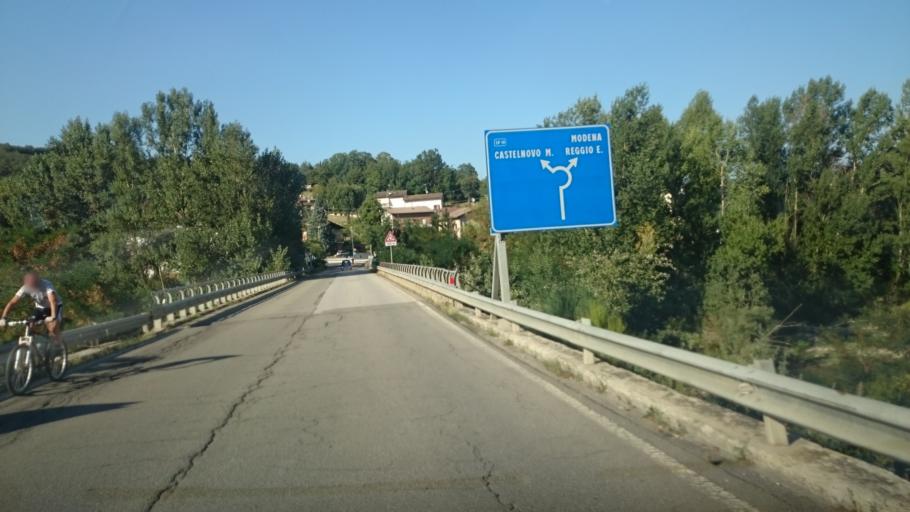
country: IT
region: Emilia-Romagna
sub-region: Provincia di Modena
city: Montefiorino
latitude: 44.4055
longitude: 10.6156
